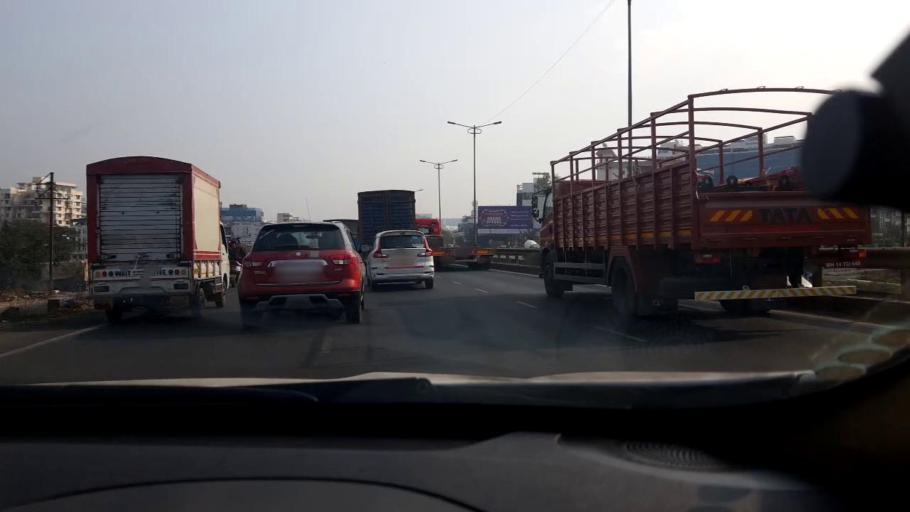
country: IN
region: Maharashtra
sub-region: Pune Division
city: Pimpri
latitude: 18.5667
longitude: 73.7668
